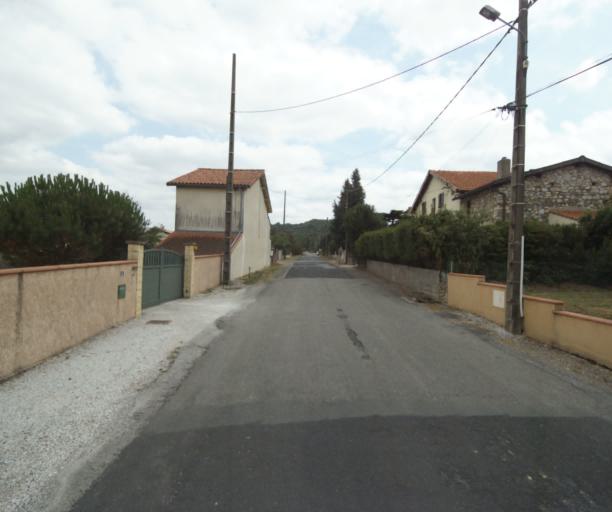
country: FR
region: Midi-Pyrenees
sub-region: Departement de la Haute-Garonne
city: Revel
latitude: 43.4494
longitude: 2.0012
